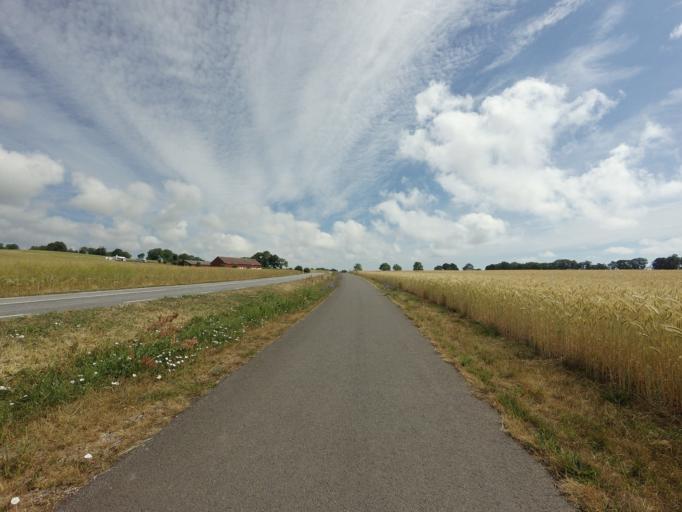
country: SE
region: Skane
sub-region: Simrishamns Kommun
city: Simrishamn
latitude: 55.4890
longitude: 14.3060
